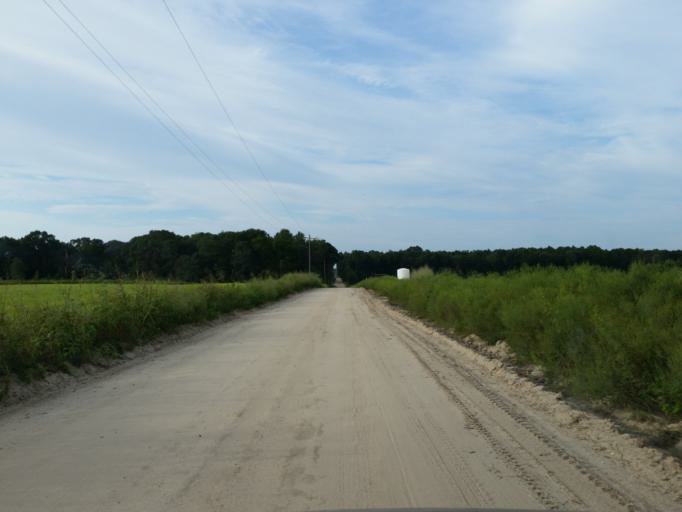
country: US
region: Florida
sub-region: Madison County
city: Madison
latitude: 30.5256
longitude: -83.2158
